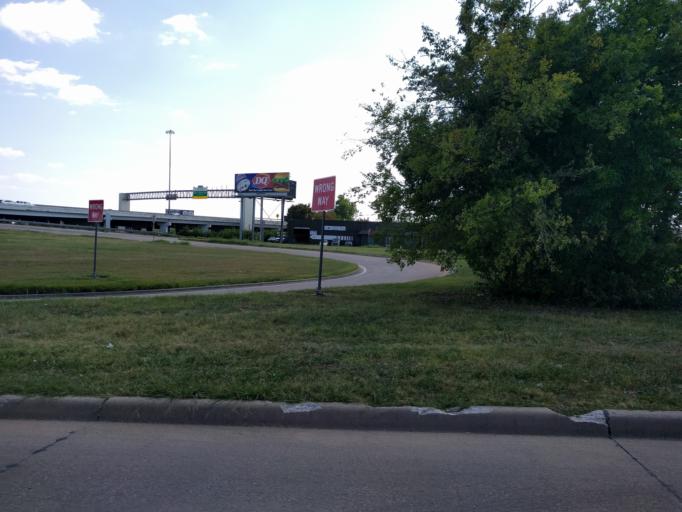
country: US
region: Texas
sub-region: Dallas County
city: Dallas
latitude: 32.7833
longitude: -96.7707
